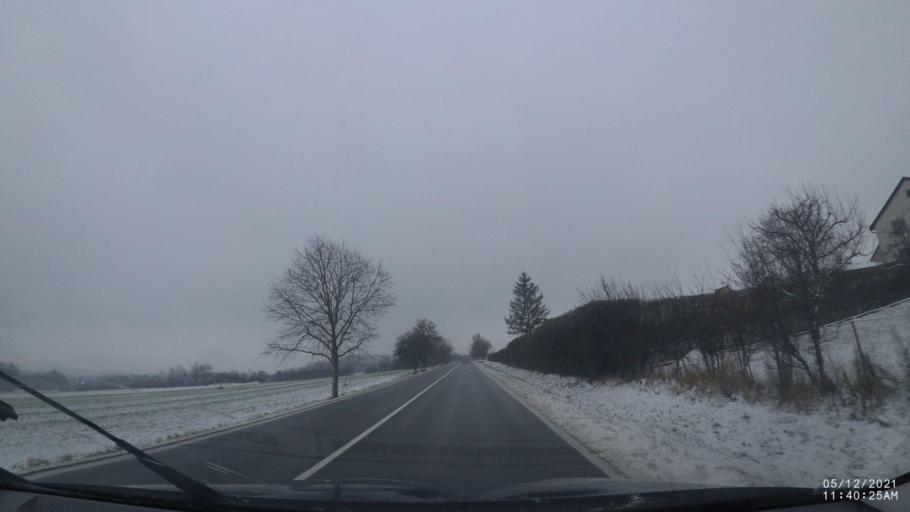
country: CZ
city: Dobruska
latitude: 50.2610
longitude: 16.2051
